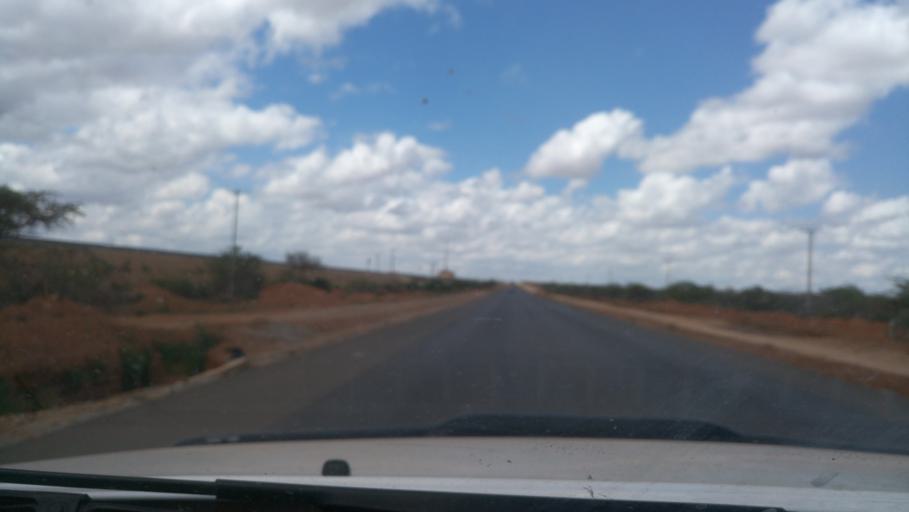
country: KE
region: Kwale
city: Mariakani
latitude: -3.7012
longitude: 38.9944
